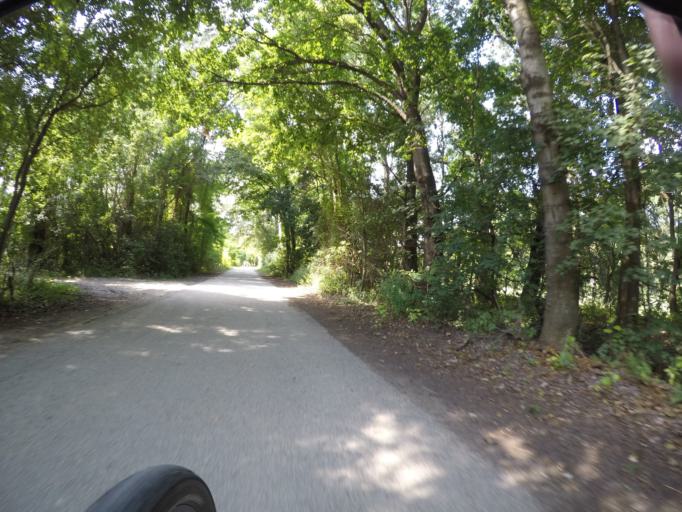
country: AT
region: Lower Austria
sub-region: Politischer Bezirk Ganserndorf
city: Gross-Enzersdorf
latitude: 48.1919
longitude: 16.5017
